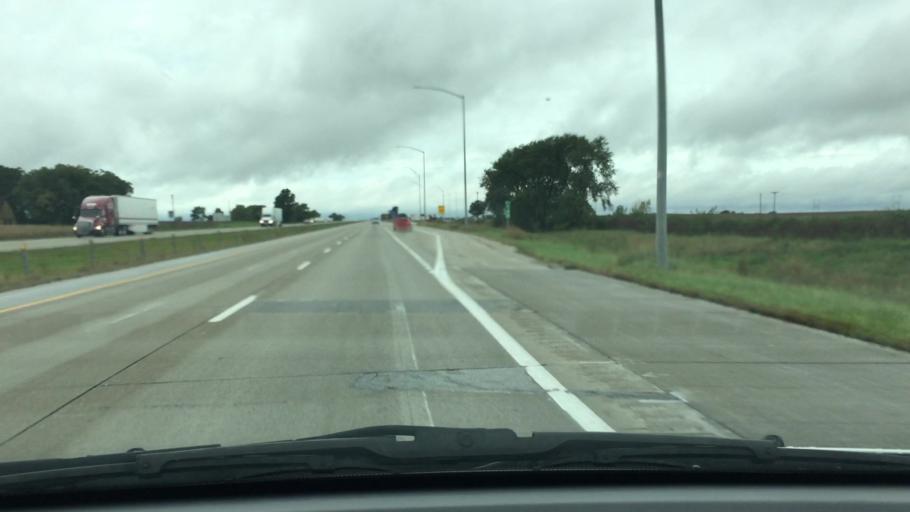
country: US
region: Iowa
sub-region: Polk County
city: Mitchellville
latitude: 41.6729
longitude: -93.3825
